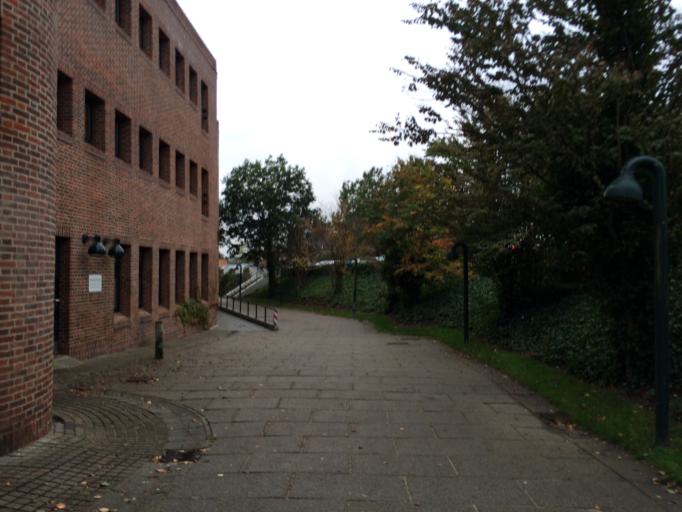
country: DK
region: Central Jutland
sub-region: Holstebro Kommune
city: Holstebro
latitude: 56.3602
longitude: 8.6151
